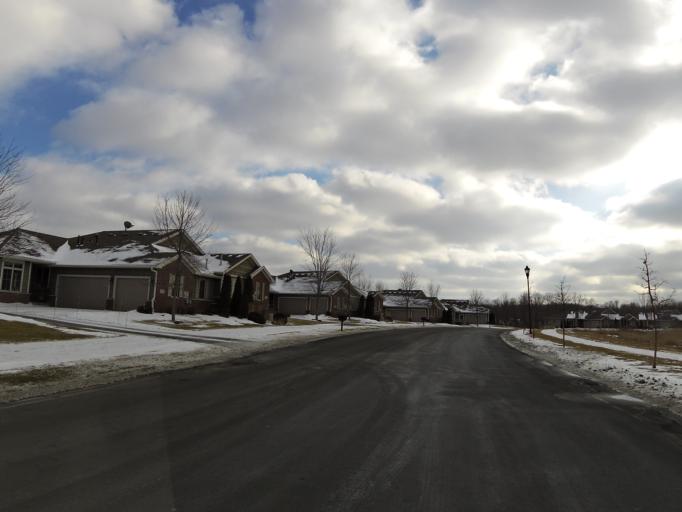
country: US
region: Minnesota
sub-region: Scott County
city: Prior Lake
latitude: 44.7452
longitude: -93.4461
